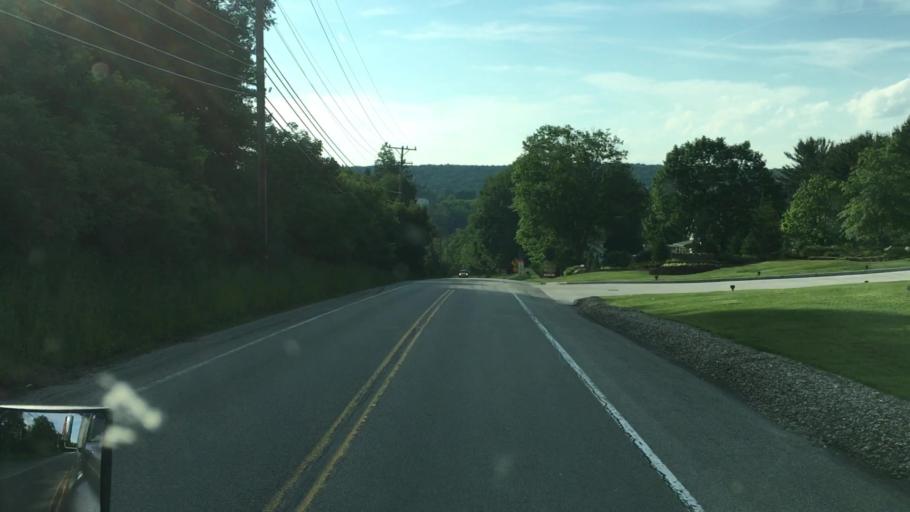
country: US
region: Pennsylvania
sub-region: Fayette County
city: Hopwood
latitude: 39.8031
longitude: -79.5557
